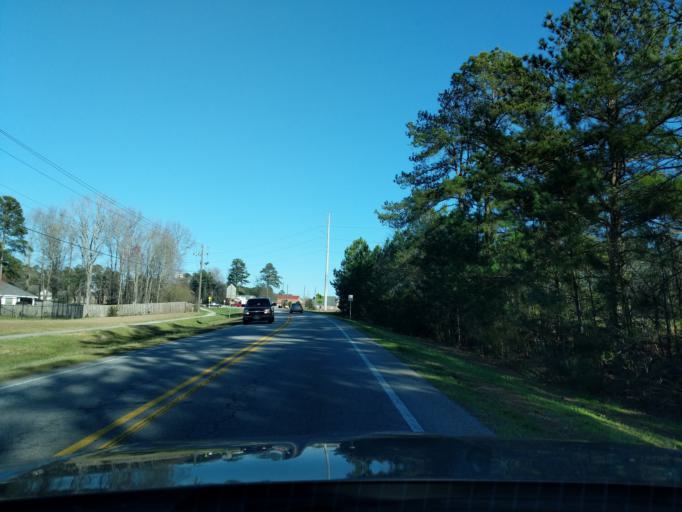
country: US
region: Georgia
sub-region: Columbia County
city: Grovetown
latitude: 33.4516
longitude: -82.2158
